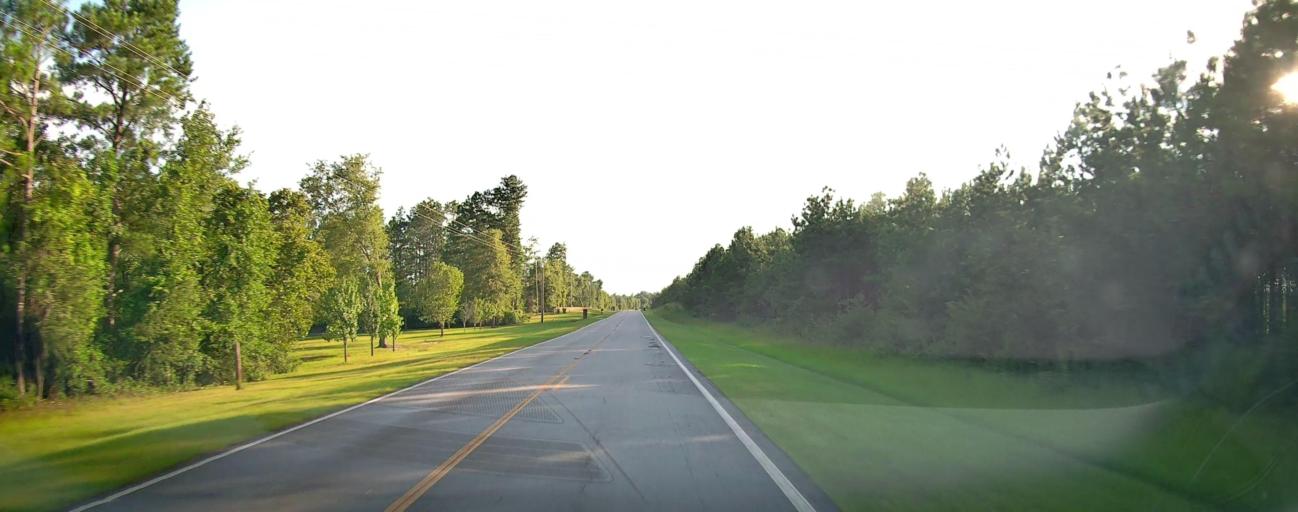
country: US
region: Georgia
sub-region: Peach County
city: Byron
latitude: 32.7107
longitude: -83.7967
